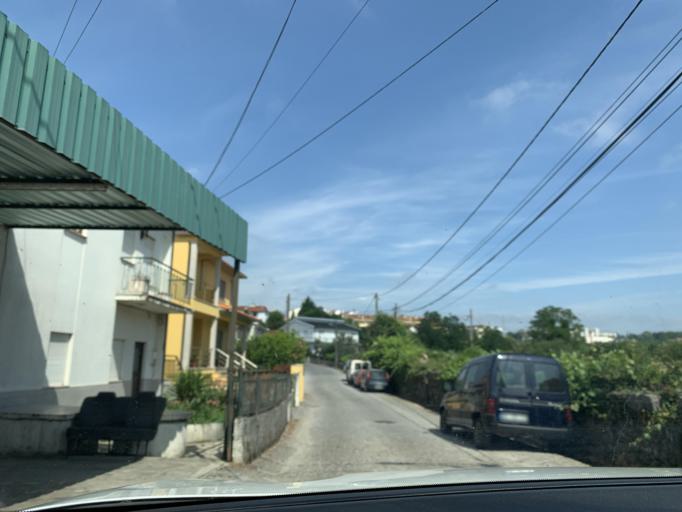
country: PT
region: Viseu
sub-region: Viseu
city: Viseu
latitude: 40.6434
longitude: -7.9007
